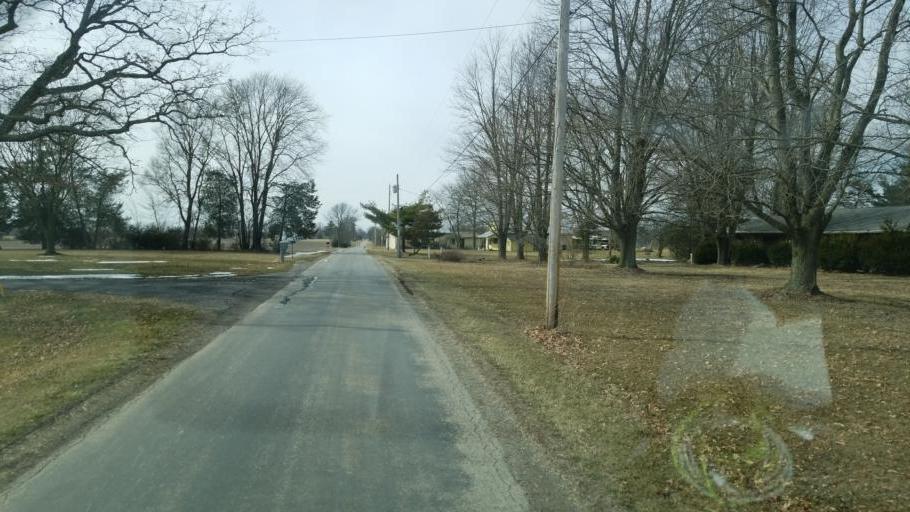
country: US
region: Ohio
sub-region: Marion County
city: Prospect
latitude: 40.3198
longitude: -83.2078
